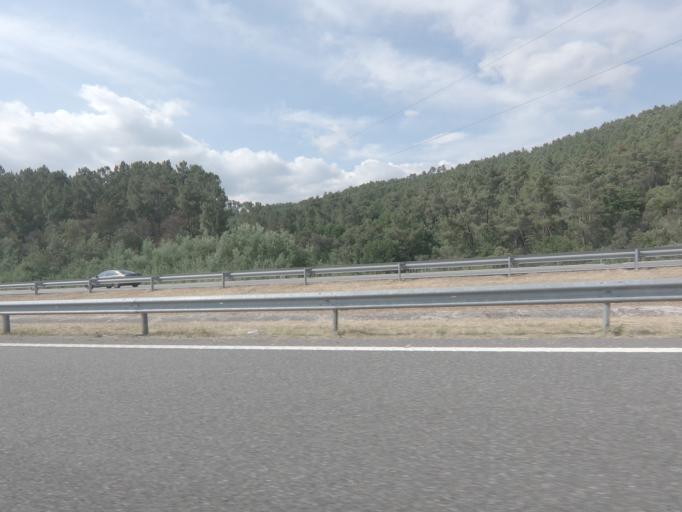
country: ES
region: Galicia
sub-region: Provincia de Ourense
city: Beade
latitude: 42.3078
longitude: -8.1055
